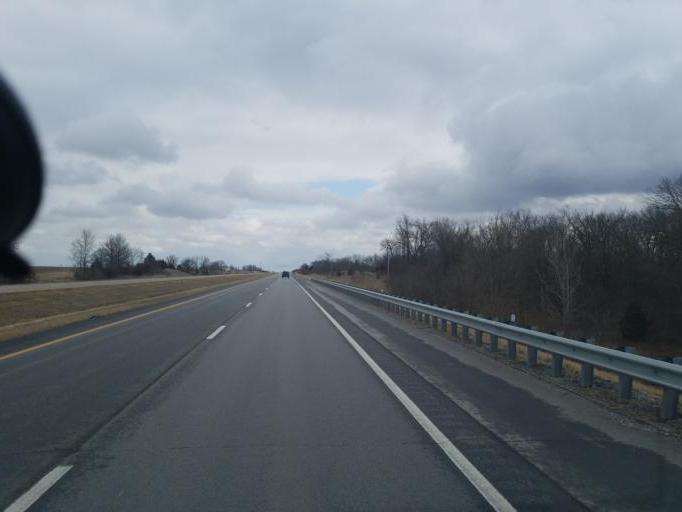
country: US
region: Missouri
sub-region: Randolph County
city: Moberly
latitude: 39.2907
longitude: -92.3704
